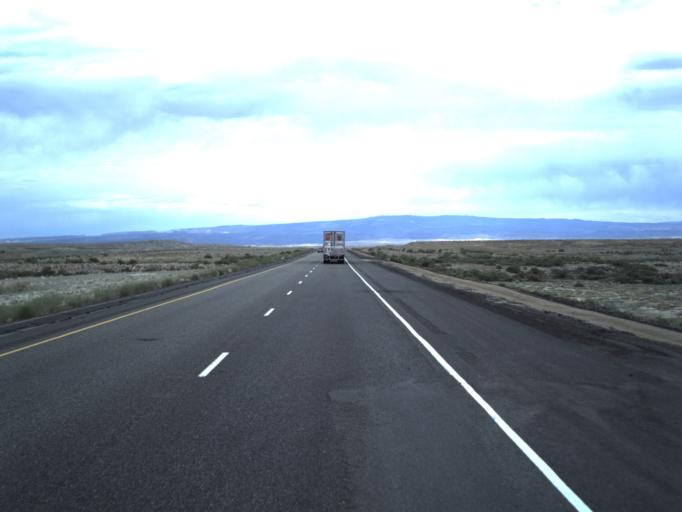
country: US
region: Utah
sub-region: Grand County
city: Moab
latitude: 38.9373
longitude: -109.4880
